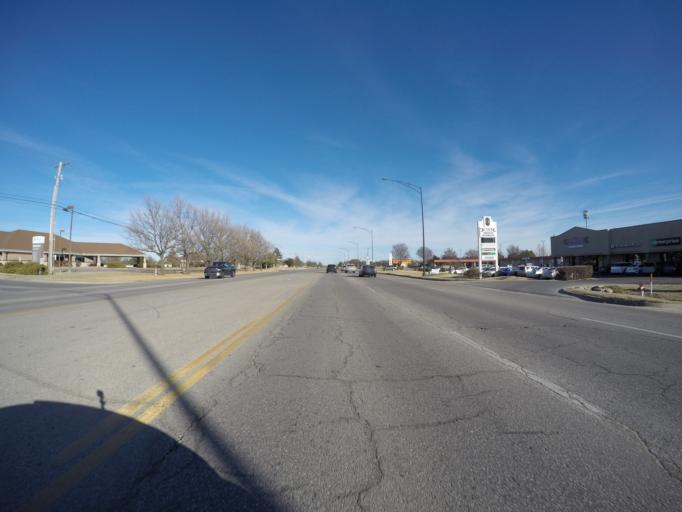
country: US
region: Kansas
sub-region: Sedgwick County
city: Maize
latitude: 37.7231
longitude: -97.4418
